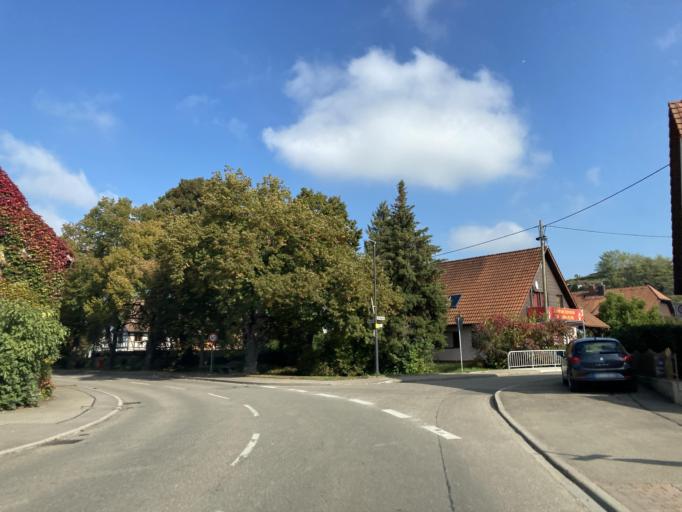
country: DE
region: Baden-Wuerttemberg
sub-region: Freiburg Region
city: Buggingen
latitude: 47.8487
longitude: 7.6377
